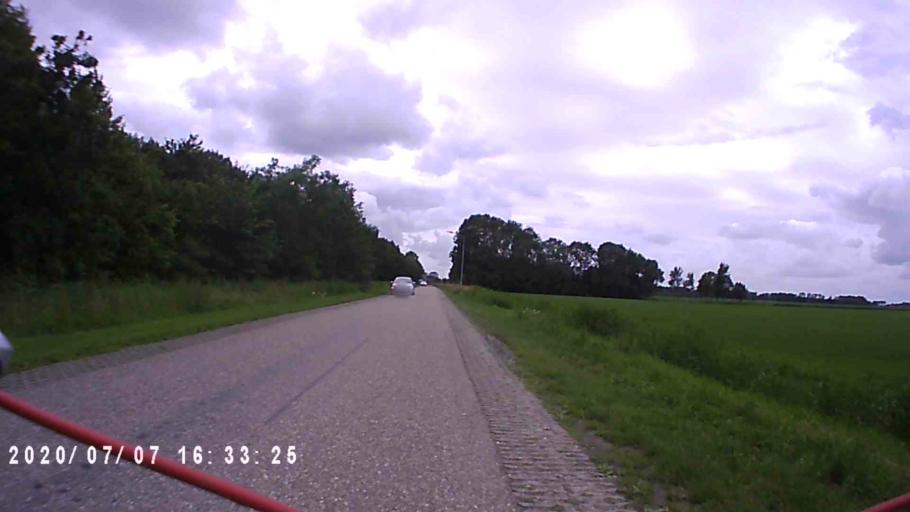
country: NL
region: Groningen
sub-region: Gemeente Winsum
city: Winsum
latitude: 53.3574
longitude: 6.5375
